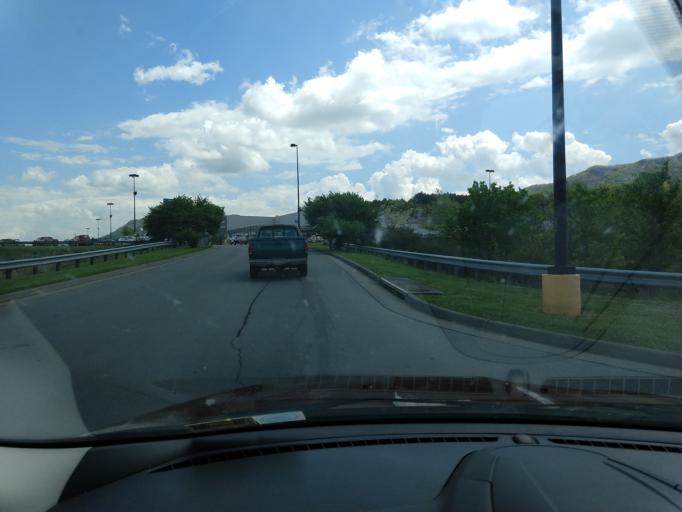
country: US
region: Virginia
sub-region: Tazewell County
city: Claypool Hill
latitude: 37.0656
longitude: -81.7340
